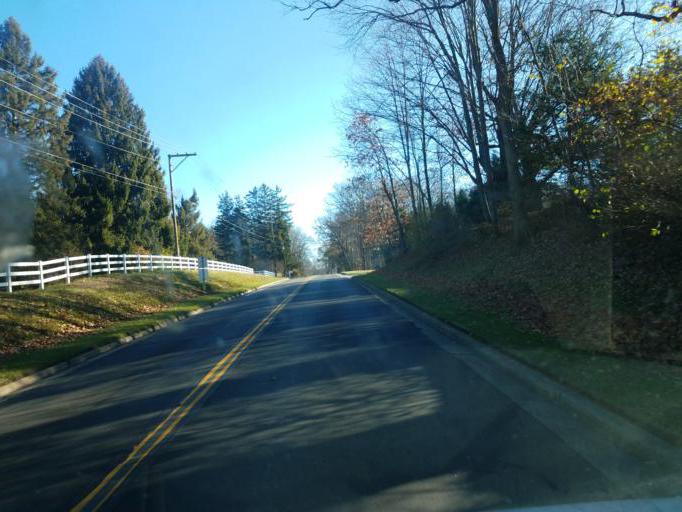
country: US
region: Ohio
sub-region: Knox County
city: Mount Vernon
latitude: 40.3884
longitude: -82.4588
